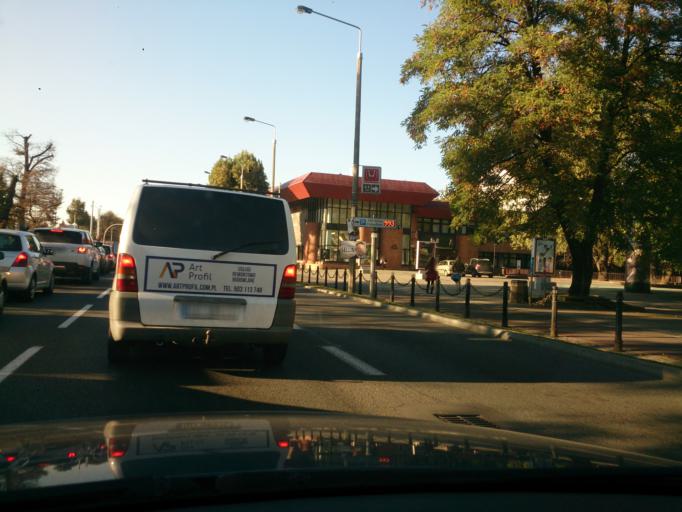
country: PL
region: Pomeranian Voivodeship
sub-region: Gdansk
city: Gdansk
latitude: 54.3717
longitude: 18.6260
